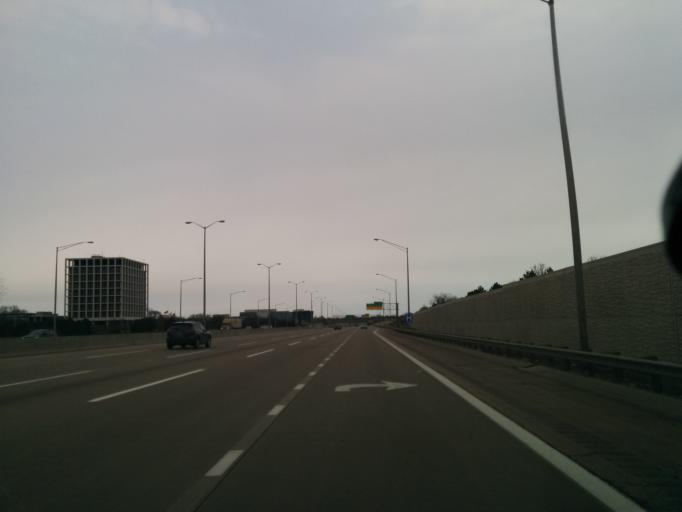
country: US
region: Illinois
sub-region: Cook County
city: Northbrook
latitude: 42.0978
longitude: -87.8679
